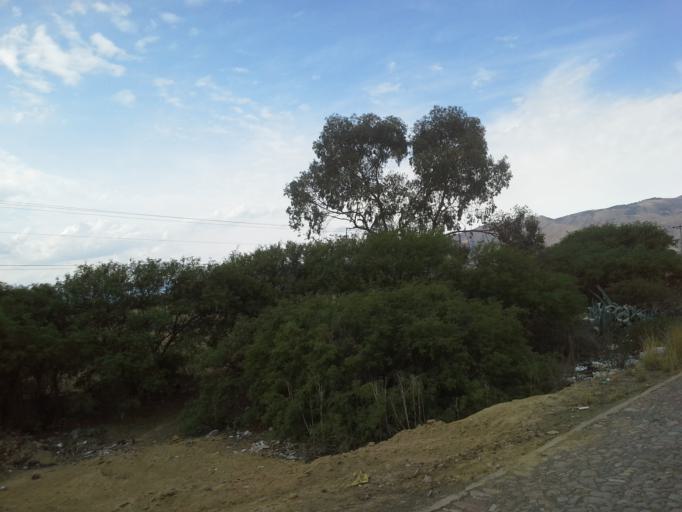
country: BO
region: Cochabamba
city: Tarata
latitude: -17.6024
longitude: -66.0196
